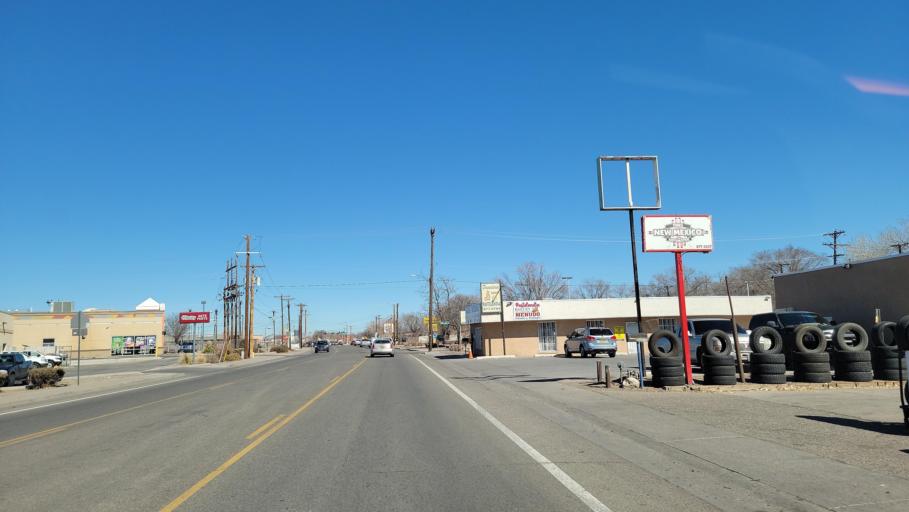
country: US
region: New Mexico
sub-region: Bernalillo County
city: South Valley
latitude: 35.0238
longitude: -106.6813
